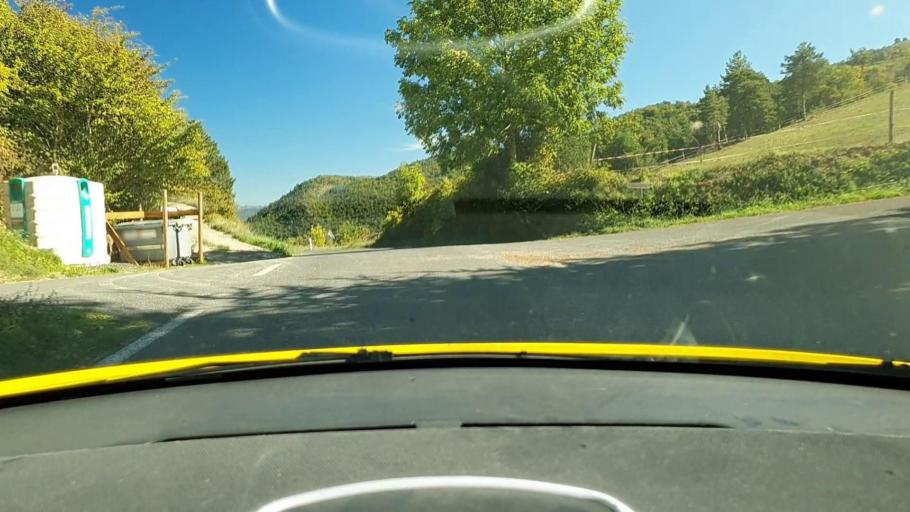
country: FR
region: Languedoc-Roussillon
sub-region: Departement du Gard
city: Le Vigan
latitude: 43.9701
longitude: 3.4495
